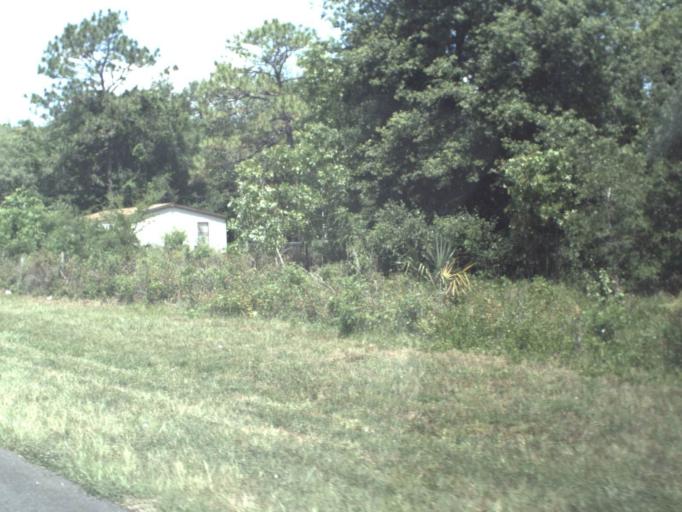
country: US
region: Florida
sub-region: Putnam County
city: Interlachen
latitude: 29.6244
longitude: -81.9085
